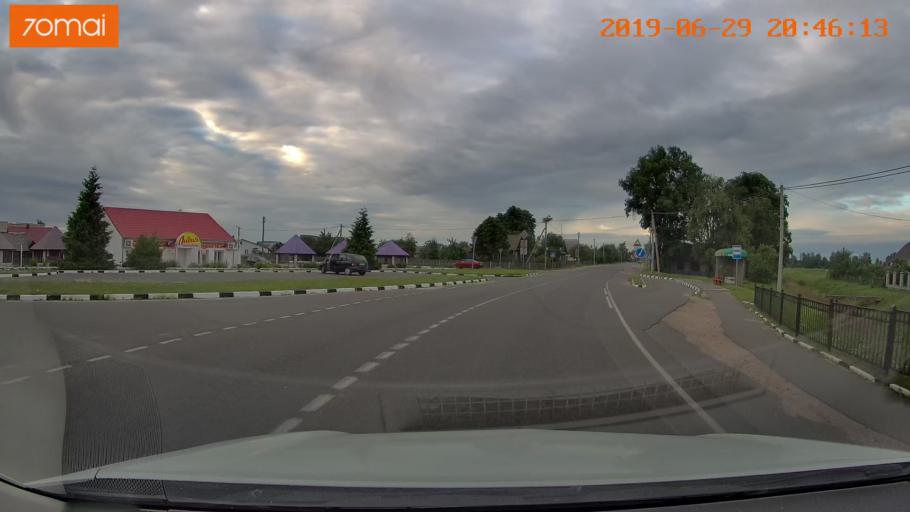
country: BY
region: Brest
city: Hantsavichy
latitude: 52.6296
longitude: 26.3076
